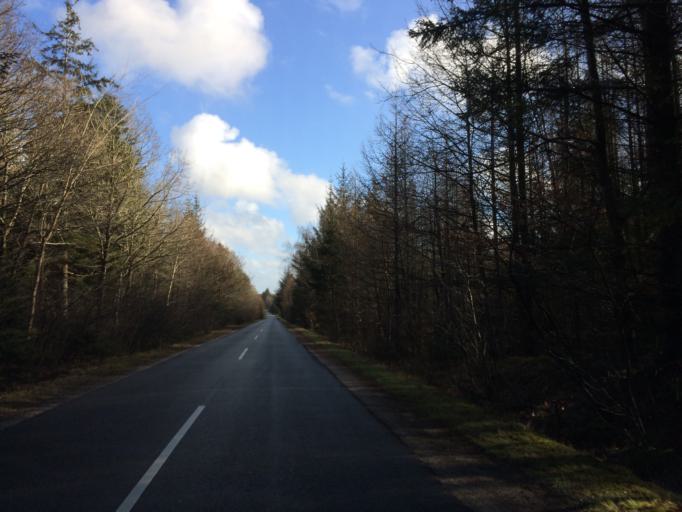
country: DK
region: Central Jutland
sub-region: Holstebro Kommune
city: Ulfborg
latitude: 56.2522
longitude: 8.3659
